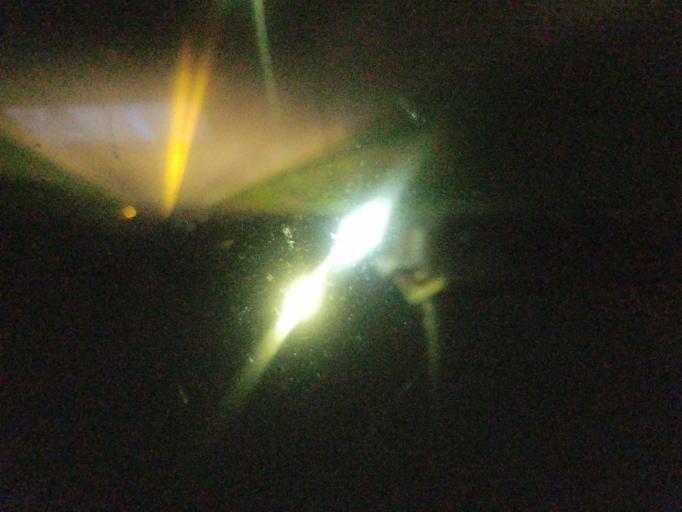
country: US
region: Kentucky
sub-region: Hart County
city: Munfordville
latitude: 37.2843
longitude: -85.9340
